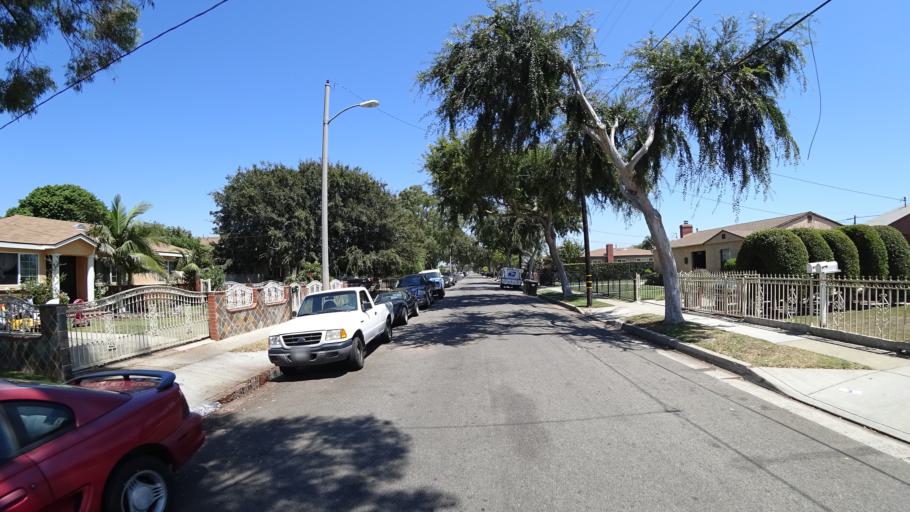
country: US
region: California
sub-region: Los Angeles County
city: Lennox
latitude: 33.9329
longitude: -118.3422
